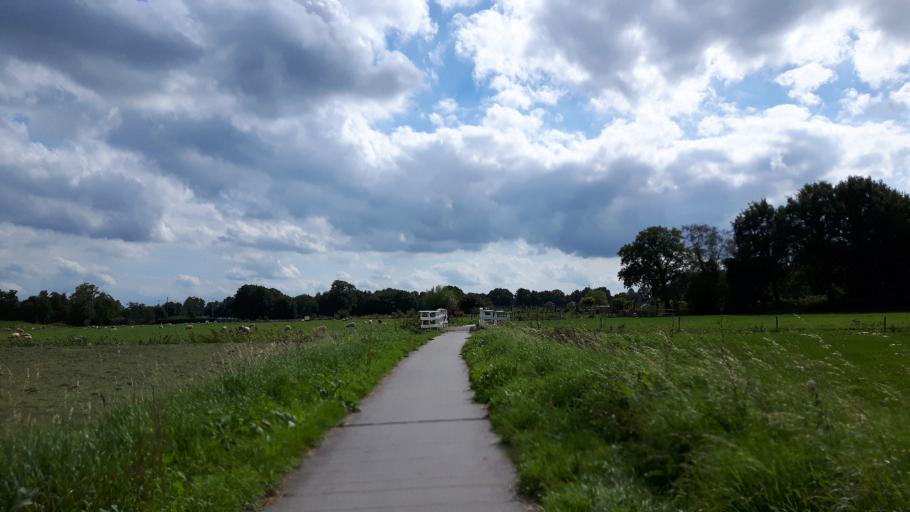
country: NL
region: Friesland
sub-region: Gemeente Heerenveen
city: Jubbega
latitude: 53.0026
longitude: 6.2914
